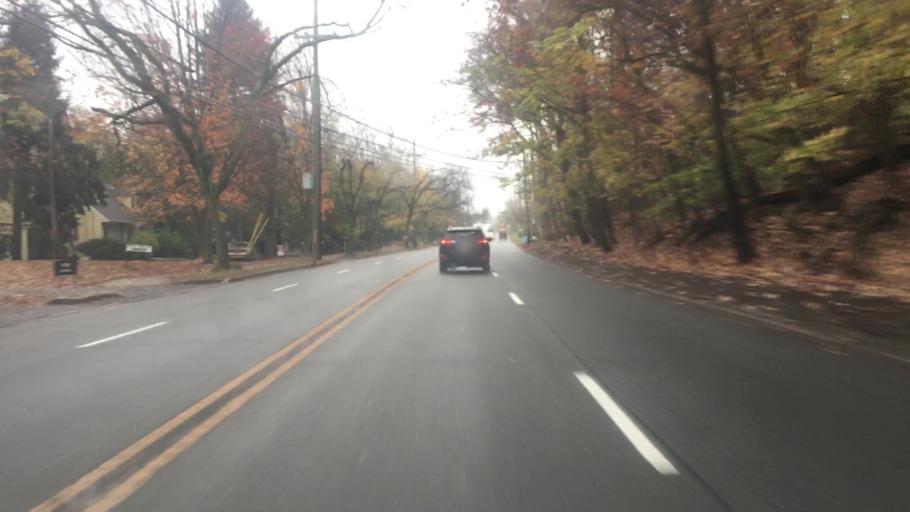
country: US
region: New Jersey
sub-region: Bergen County
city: Oakland
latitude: 40.9711
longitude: -74.2621
